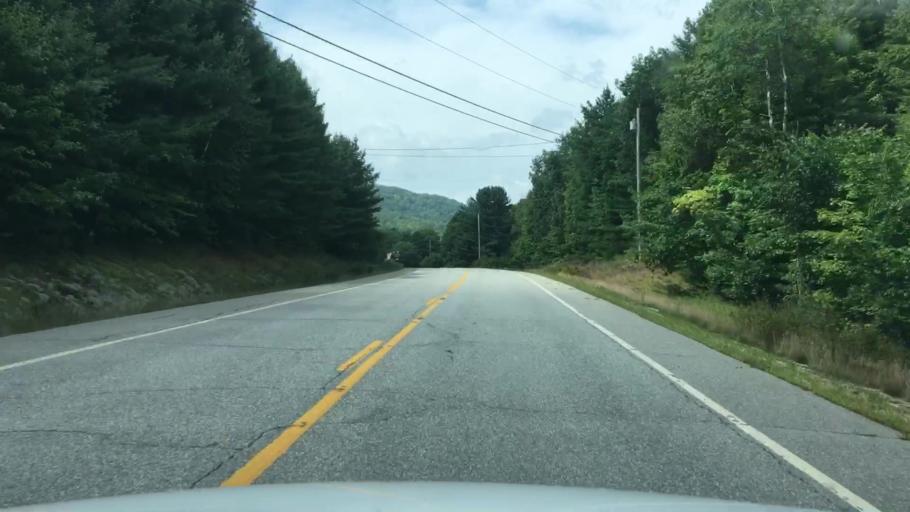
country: US
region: Maine
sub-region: Oxford County
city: Rumford
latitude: 44.5475
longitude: -70.6993
